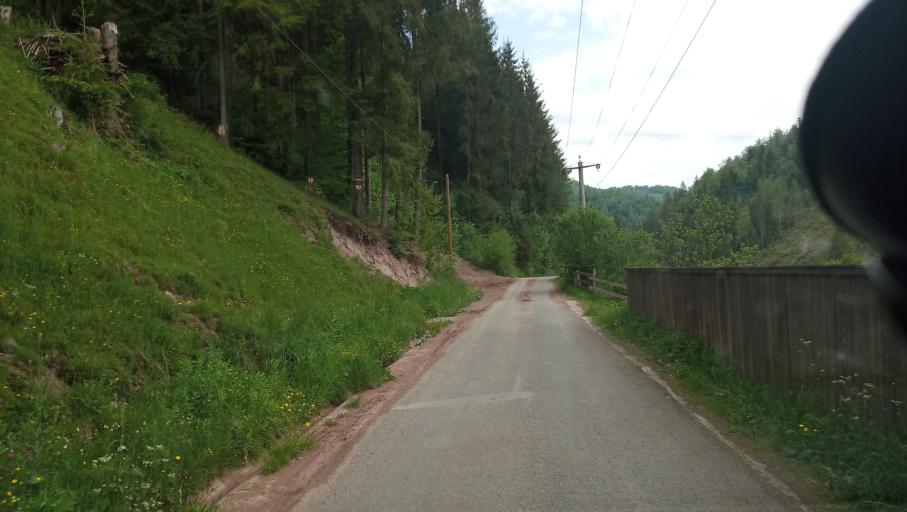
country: RO
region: Alba
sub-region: Comuna Garda de Sus
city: Garda de Sus
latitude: 46.4790
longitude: 22.7996
